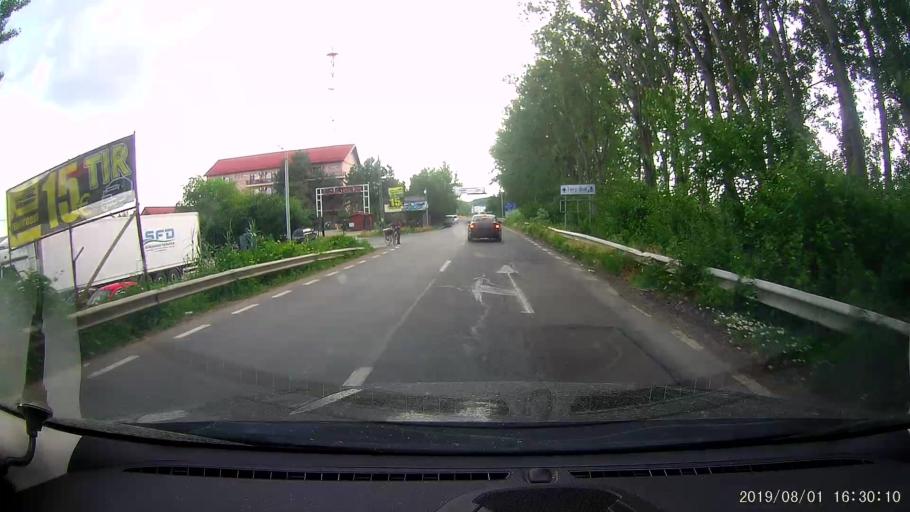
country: BG
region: Silistra
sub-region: Obshtina Silistra
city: Silistra
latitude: 44.1351
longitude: 27.2761
